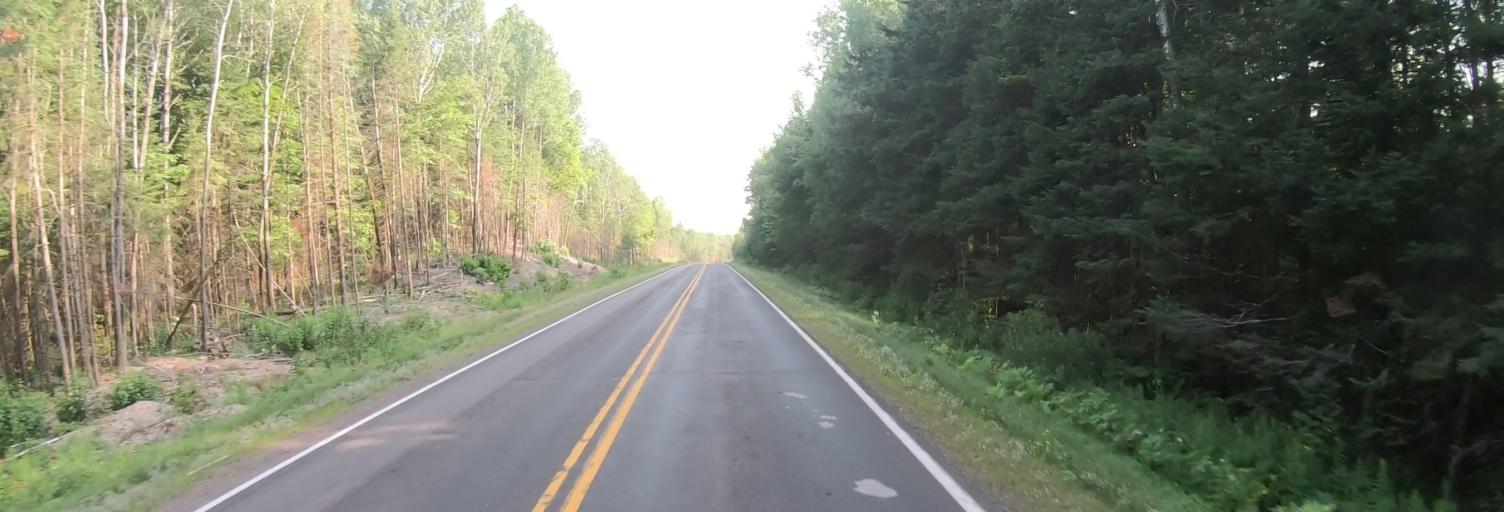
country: US
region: Wisconsin
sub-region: Ashland County
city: Ashland
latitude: 46.2733
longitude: -90.8387
